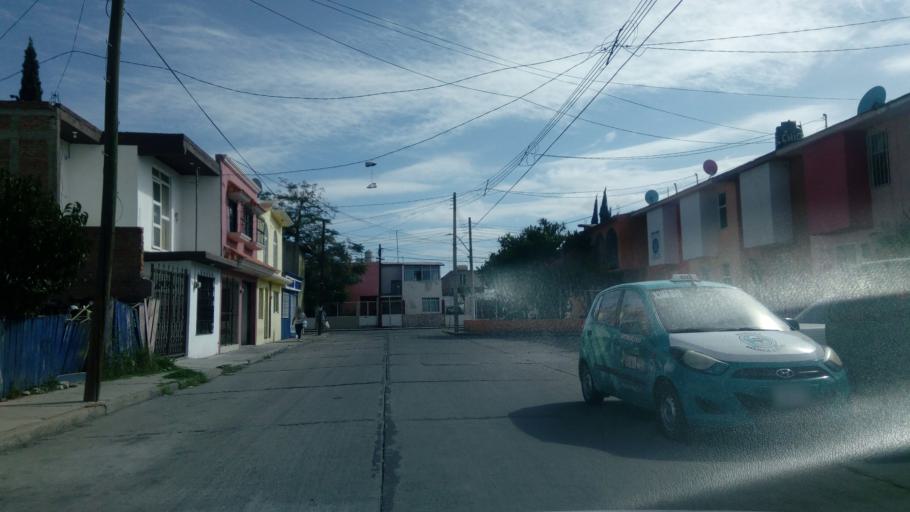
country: MX
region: Durango
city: Victoria de Durango
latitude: 24.0074
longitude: -104.6559
